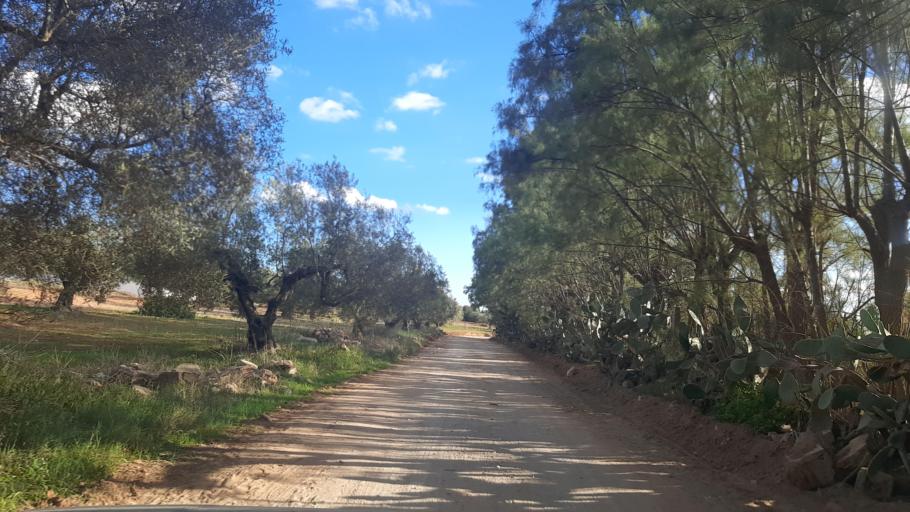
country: TN
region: Nabul
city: Al Hammamat
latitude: 36.4266
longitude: 10.5072
